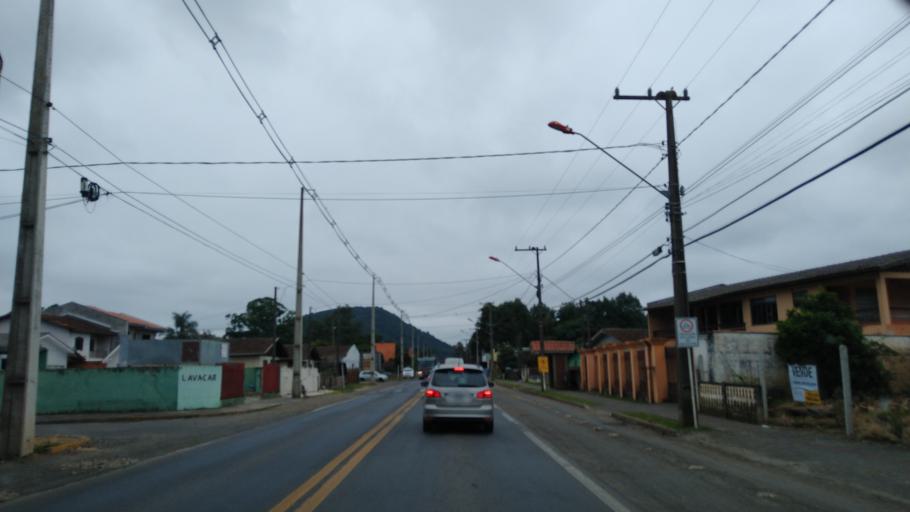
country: BR
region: Santa Catarina
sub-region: Porto Uniao
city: Porto Uniao
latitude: -26.2620
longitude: -51.0641
